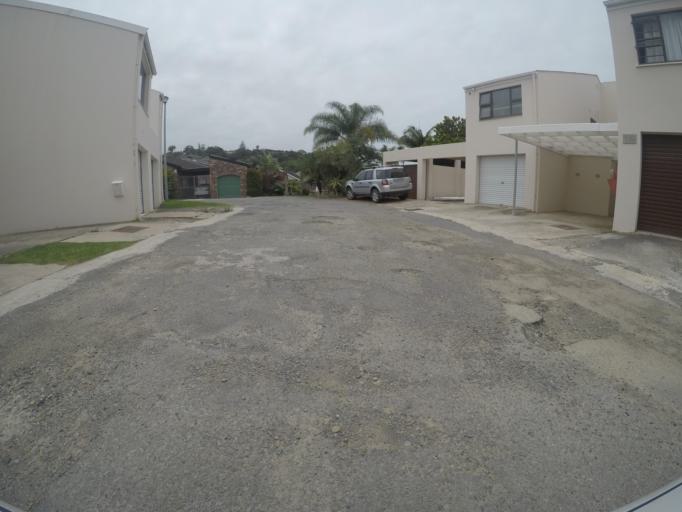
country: ZA
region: Eastern Cape
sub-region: Buffalo City Metropolitan Municipality
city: East London
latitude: -32.9819
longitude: 27.9385
